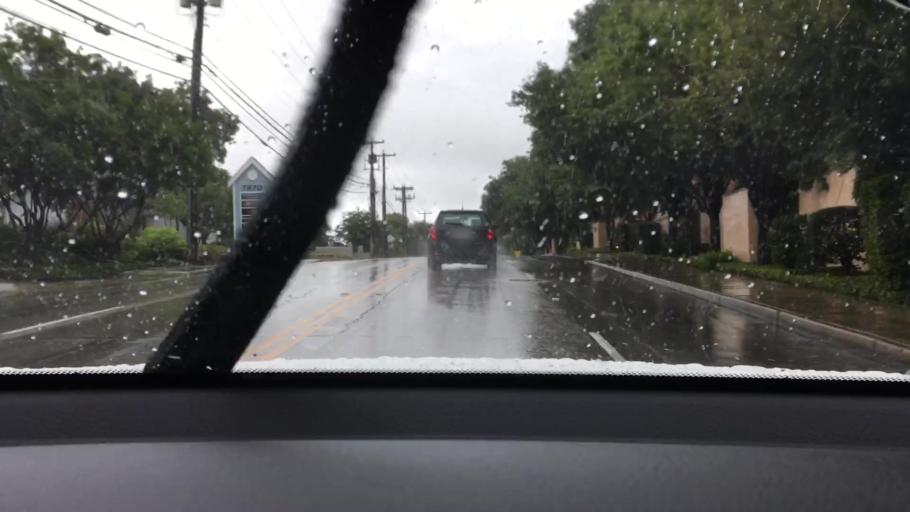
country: US
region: Texas
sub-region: Bexar County
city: Alamo Heights
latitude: 29.5054
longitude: -98.4663
